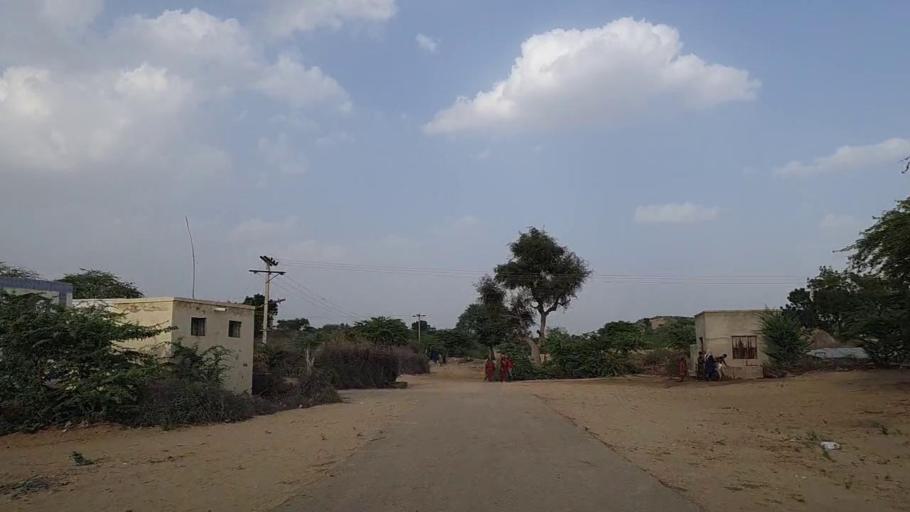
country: PK
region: Sindh
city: Islamkot
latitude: 24.7983
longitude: 70.2061
